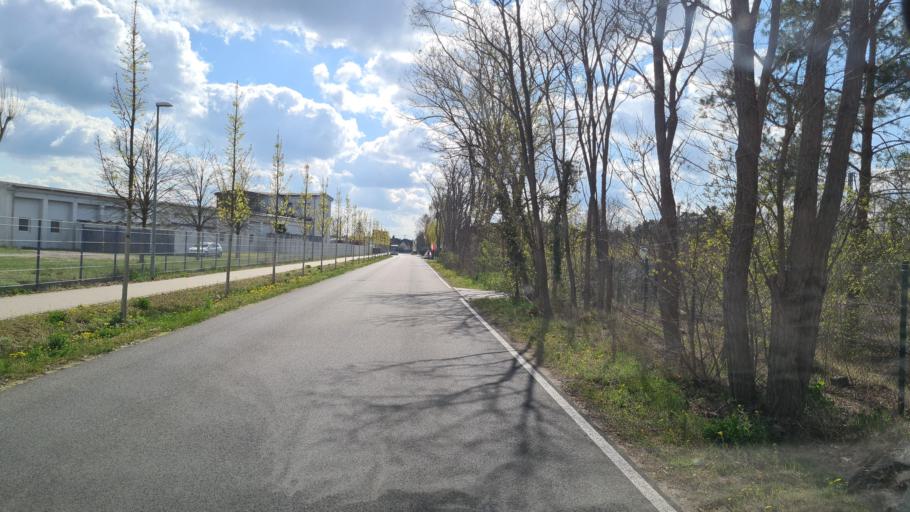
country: DE
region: Brandenburg
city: Luckenwalde
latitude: 52.0813
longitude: 13.1479
